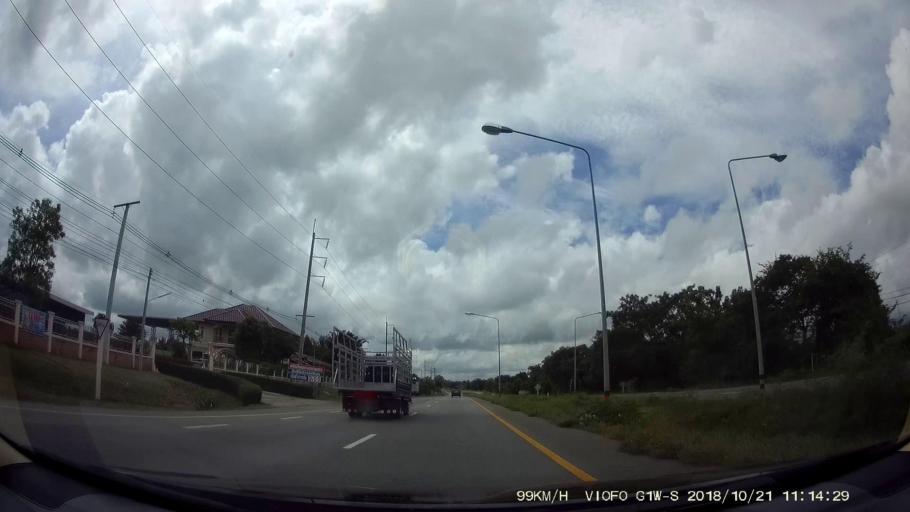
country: TH
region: Chaiyaphum
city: Chaiyaphum
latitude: 15.9039
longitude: 102.1219
